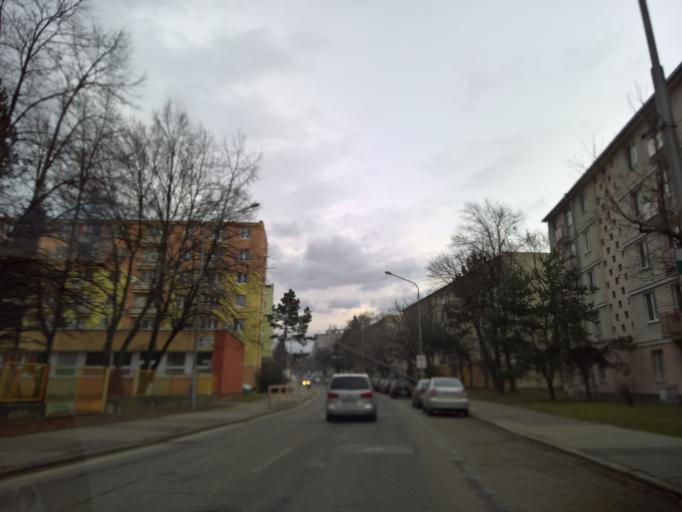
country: SK
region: Nitriansky
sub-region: Okres Nitra
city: Nitra
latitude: 48.3104
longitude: 18.0802
